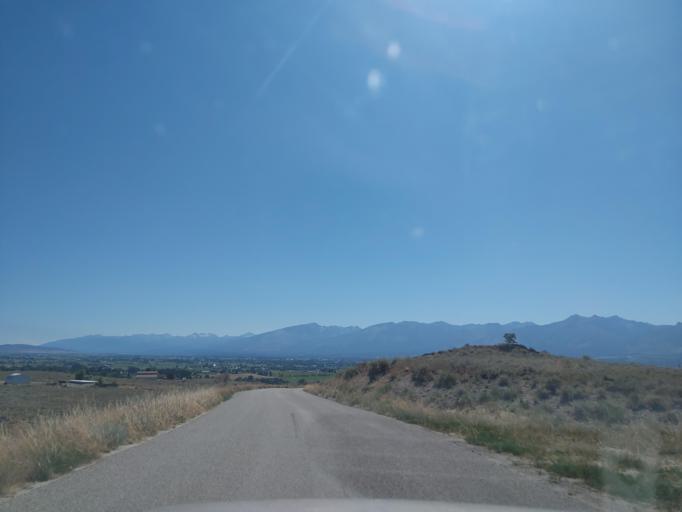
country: US
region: Montana
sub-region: Ravalli County
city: Hamilton
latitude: 46.3486
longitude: -114.0478
